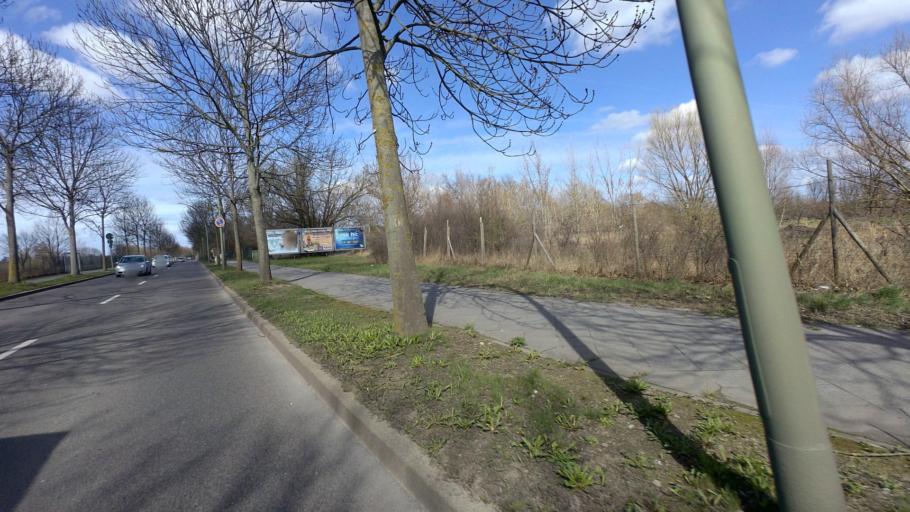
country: DE
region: Berlin
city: Blankenburg
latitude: 52.5857
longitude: 13.4593
